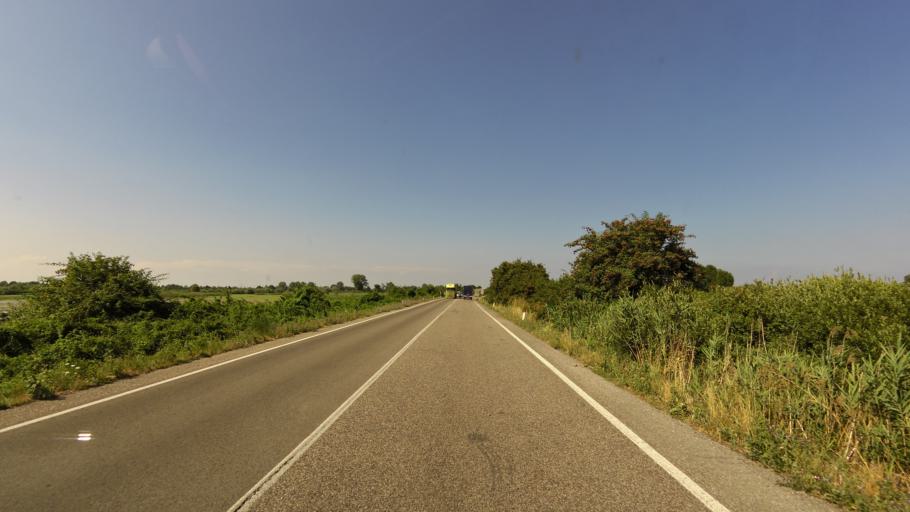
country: IT
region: Emilia-Romagna
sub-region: Provincia di Ravenna
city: Marina Romea
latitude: 44.5392
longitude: 12.2341
